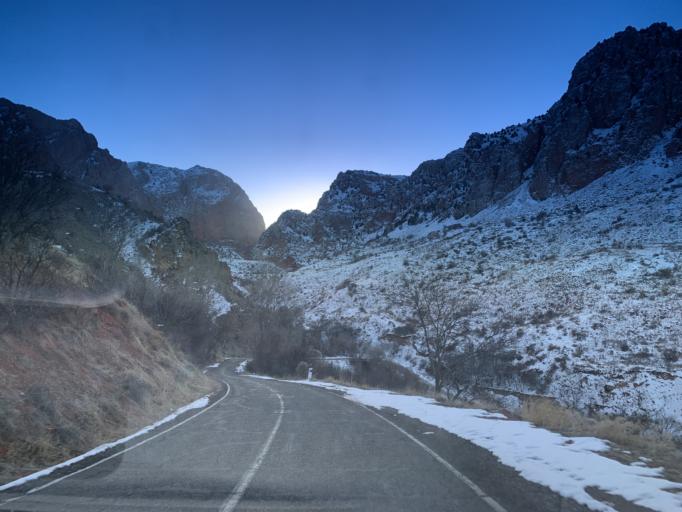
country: AM
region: Vayots' Dzori Marz
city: Areni
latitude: 39.6835
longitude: 45.2327
